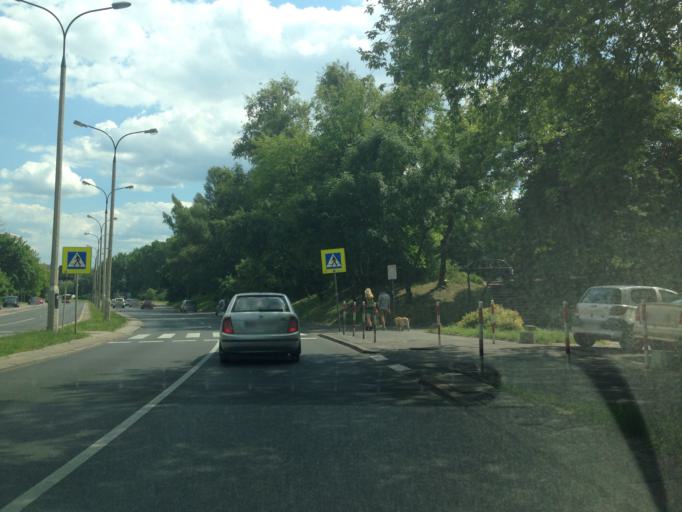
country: PL
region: Masovian Voivodeship
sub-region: Warszawa
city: Mokotow
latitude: 52.2096
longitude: 21.0256
